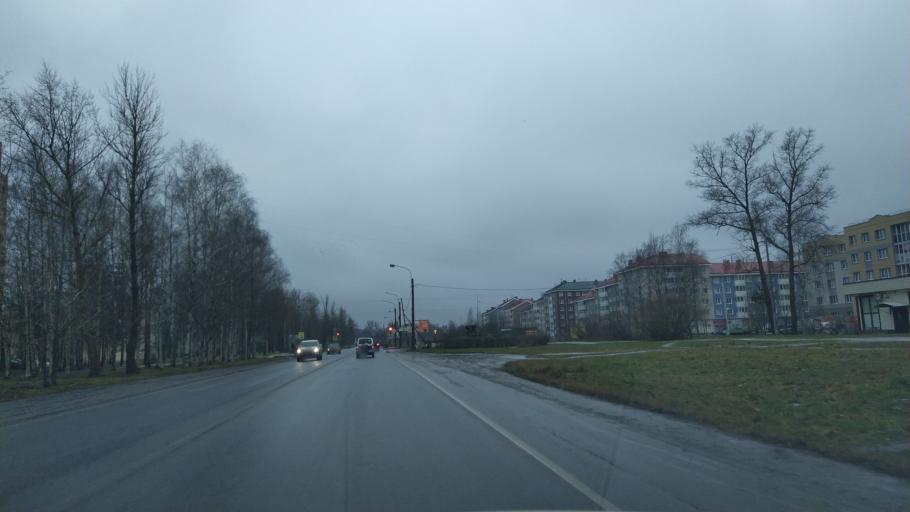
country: RU
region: St.-Petersburg
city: Tyarlevo
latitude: 59.7318
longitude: 30.4670
